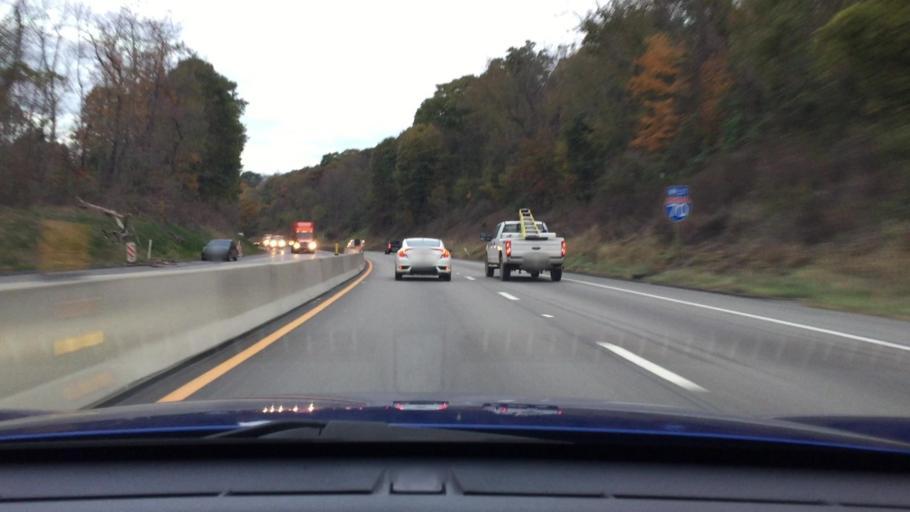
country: US
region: Pennsylvania
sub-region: Washington County
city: Bentleyville
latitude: 40.1294
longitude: -79.9627
